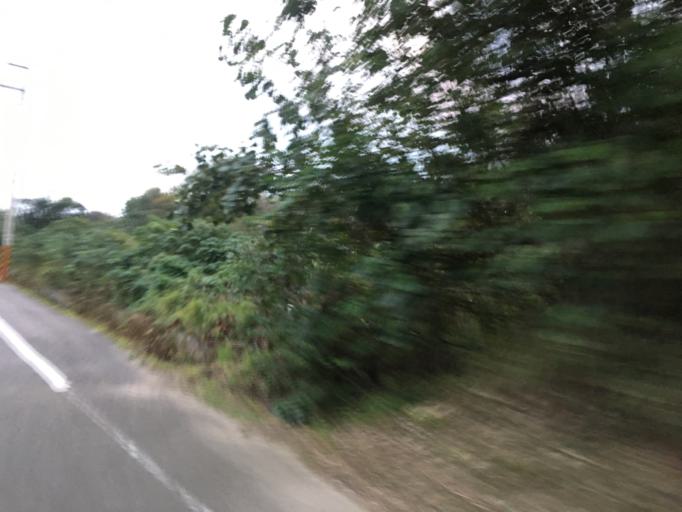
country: TW
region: Taiwan
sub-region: Hsinchu
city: Hsinchu
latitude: 24.7372
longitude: 120.8903
